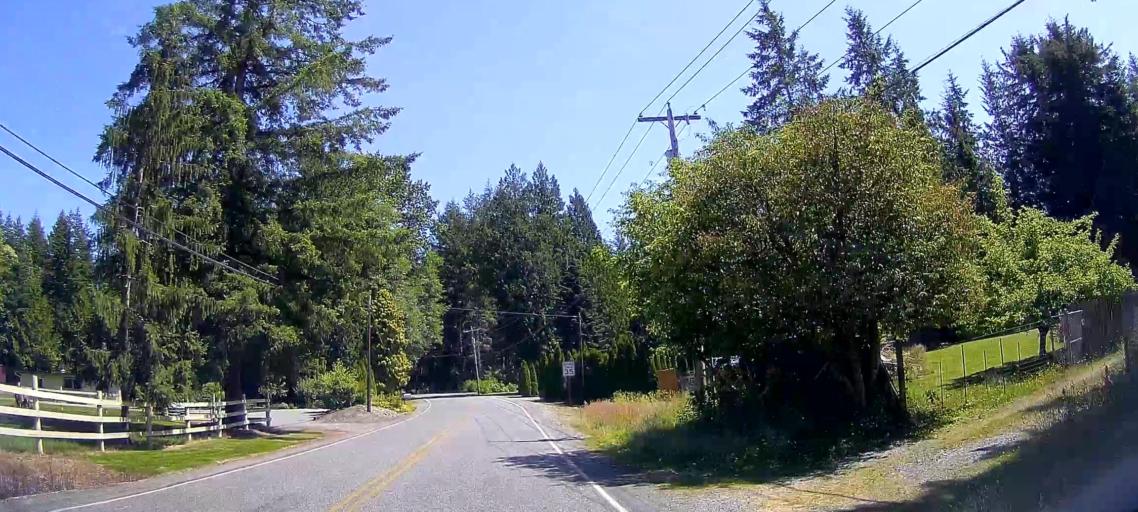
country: US
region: Washington
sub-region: Skagit County
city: Burlington
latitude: 48.5936
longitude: -122.3228
